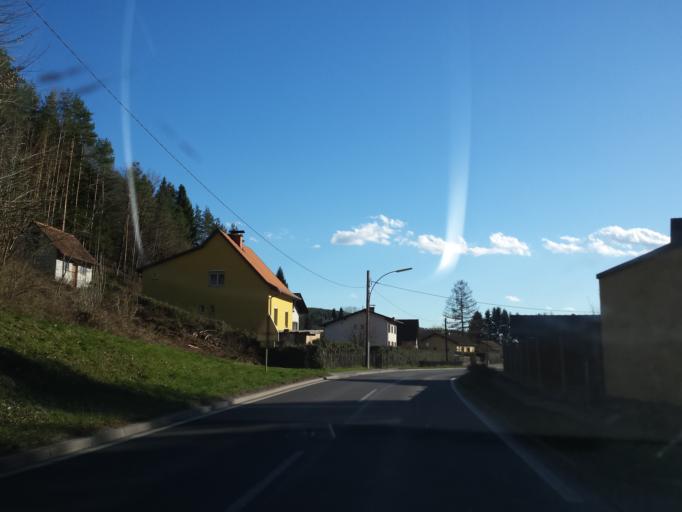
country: AT
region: Styria
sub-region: Politischer Bezirk Graz-Umgebung
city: Stattegg
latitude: 47.1269
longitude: 15.4443
